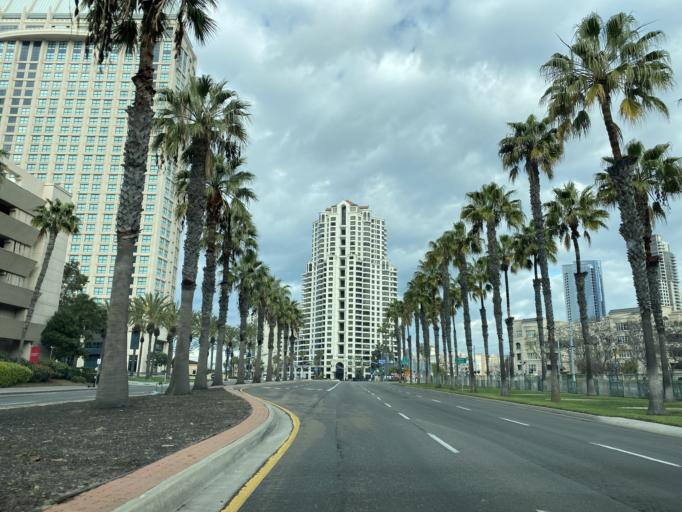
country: US
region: California
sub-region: San Diego County
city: San Diego
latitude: 32.7104
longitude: -117.1668
